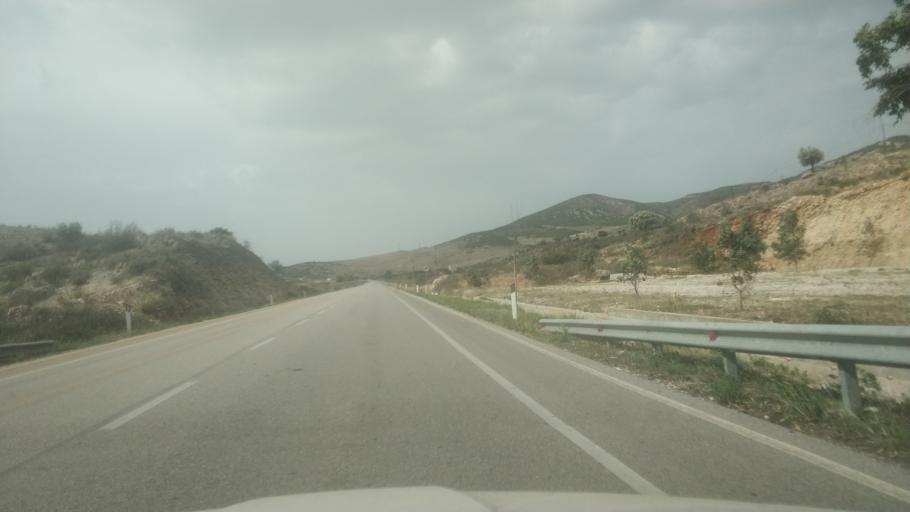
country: AL
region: Gjirokaster
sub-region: Rrethi i Tepelenes
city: Memaliaj
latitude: 40.3573
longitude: 19.9338
